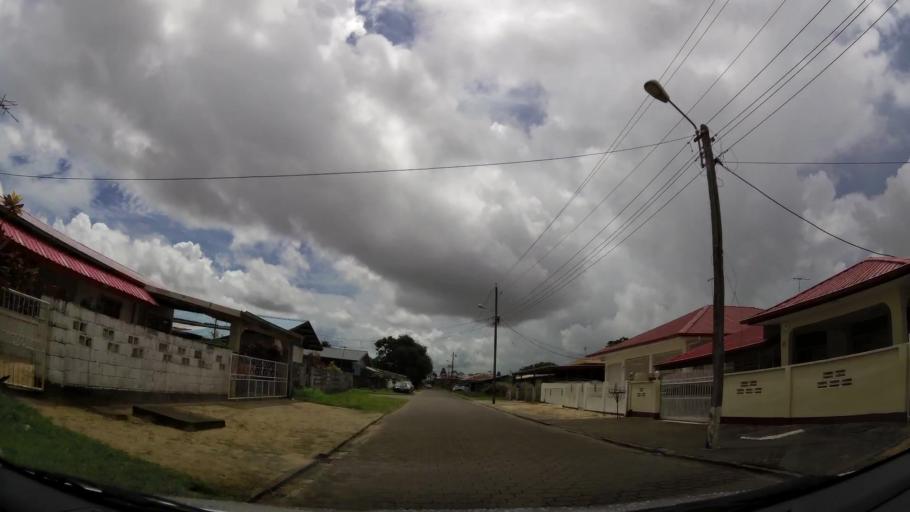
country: SR
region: Paramaribo
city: Paramaribo
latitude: 5.8272
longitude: -55.2248
